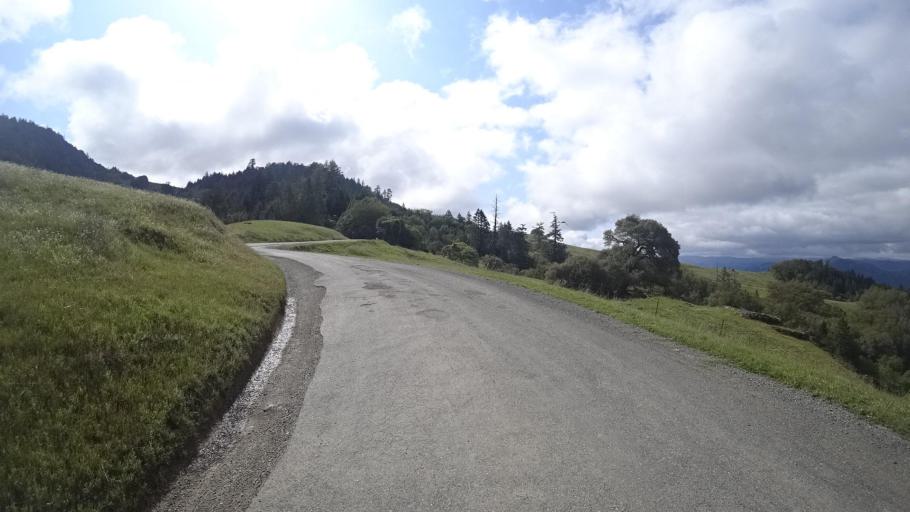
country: US
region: California
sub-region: Humboldt County
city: Redway
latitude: 40.1610
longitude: -123.5637
